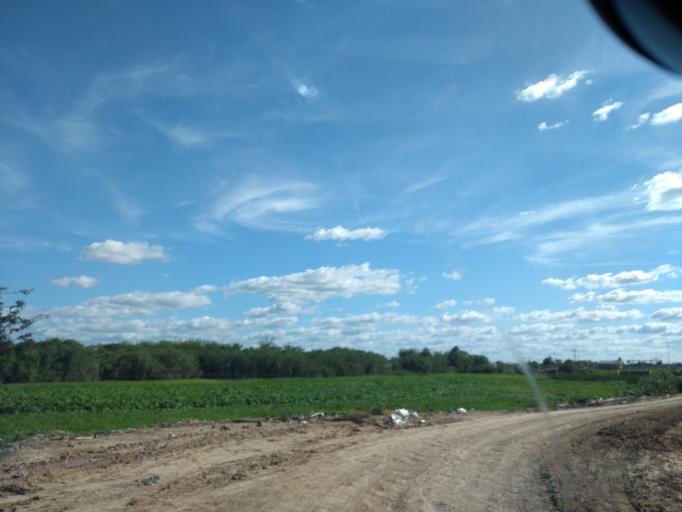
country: AR
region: Chaco
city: Resistencia
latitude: -27.4535
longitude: -58.9612
